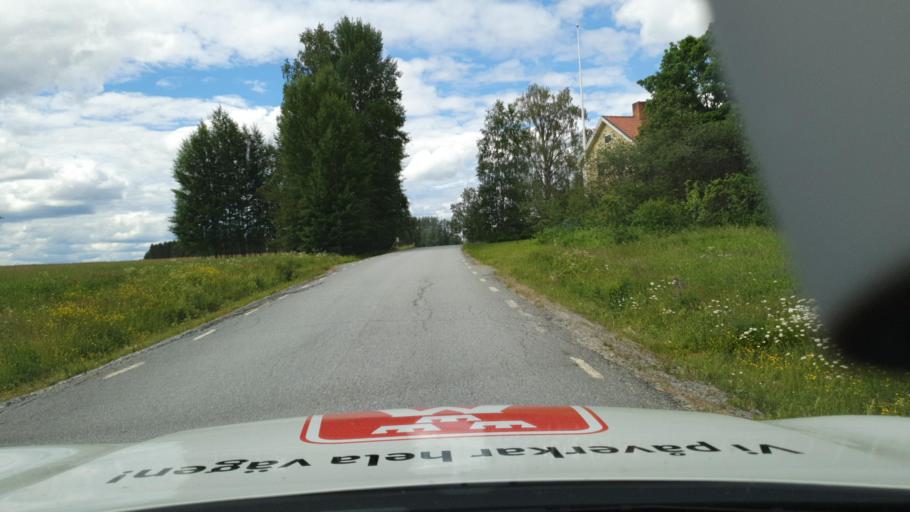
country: SE
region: Vaesterbotten
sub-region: Bjurholms Kommun
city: Bjurholm
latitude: 63.9146
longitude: 19.0776
